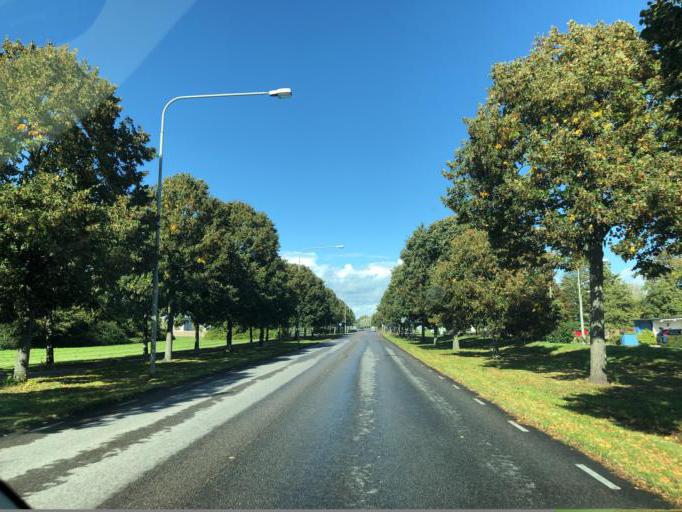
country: SE
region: Skane
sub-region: Landskrona
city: Landskrona
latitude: 55.8925
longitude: 12.8285
